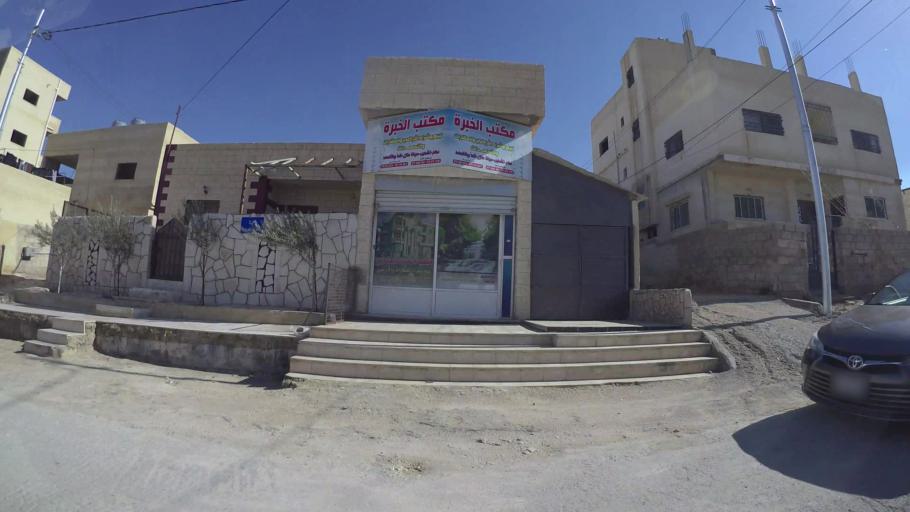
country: JO
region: Zarqa
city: Russeifa
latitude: 32.0412
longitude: 36.0365
